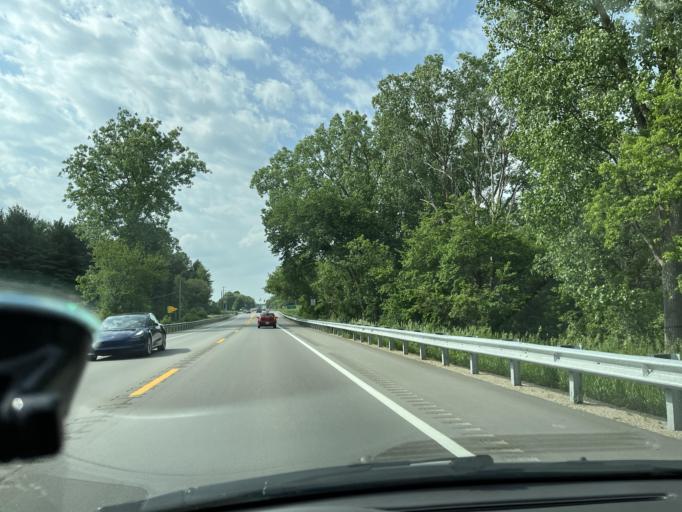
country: US
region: Michigan
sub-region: Barry County
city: Middleville
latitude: 42.7233
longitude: -85.4746
